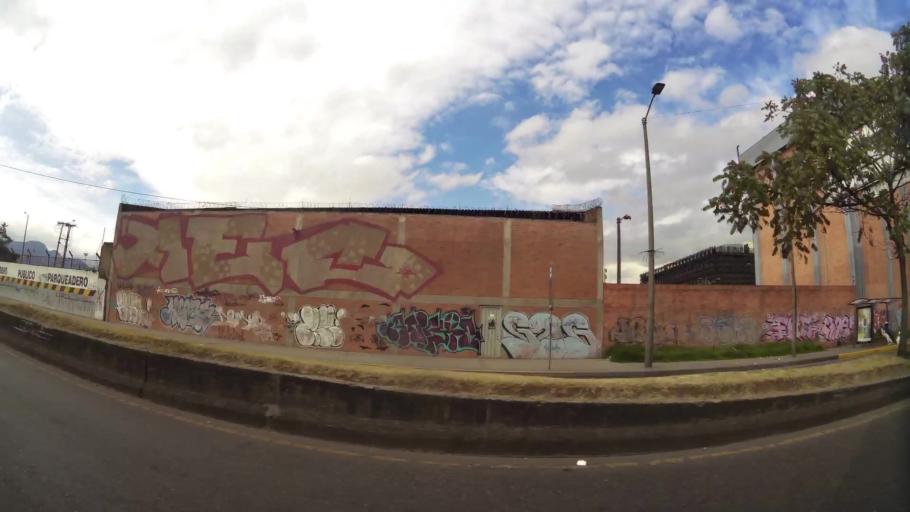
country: CO
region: Bogota D.C.
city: Bogota
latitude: 4.6202
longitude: -74.0902
